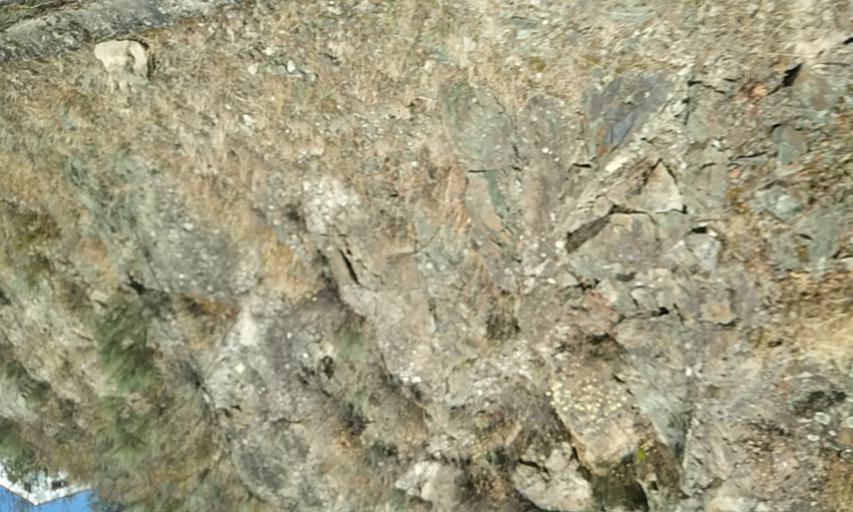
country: PT
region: Viseu
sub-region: Sao Joao da Pesqueira
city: Sao Joao da Pesqueira
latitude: 41.1825
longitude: -7.4397
